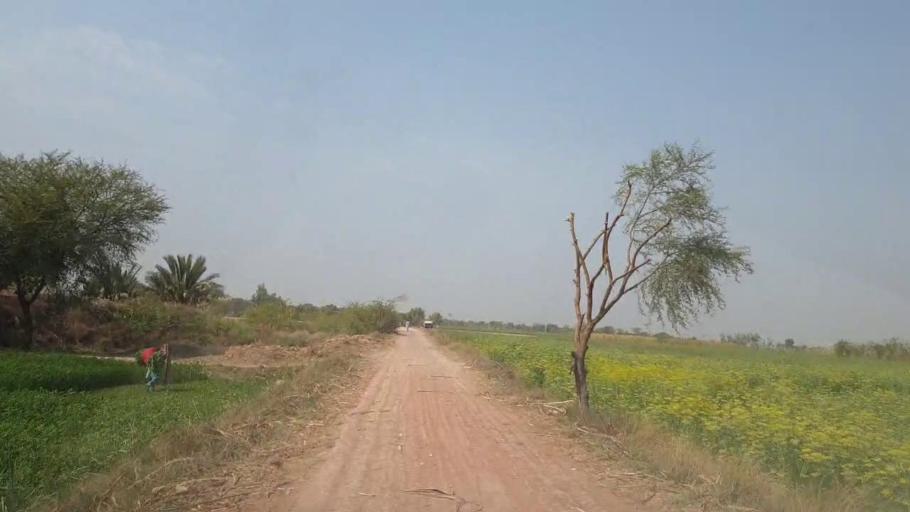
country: PK
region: Sindh
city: Mirpur Khas
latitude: 25.5789
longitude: 69.1356
